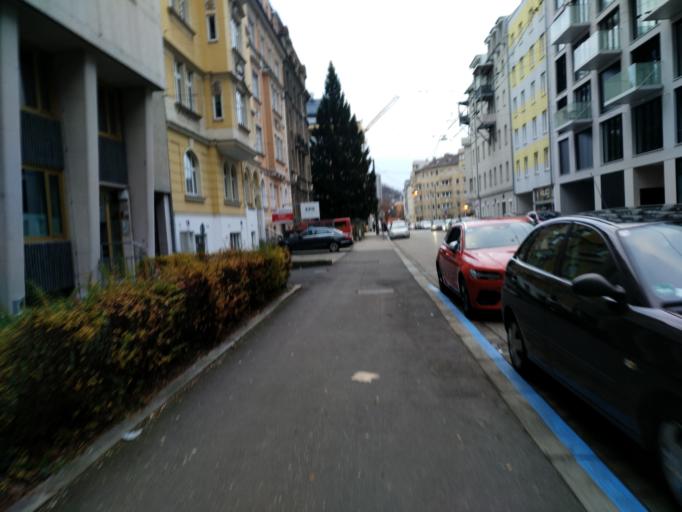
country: AT
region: Upper Austria
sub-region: Linz Stadt
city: Linz
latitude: 48.2942
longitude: 14.2902
